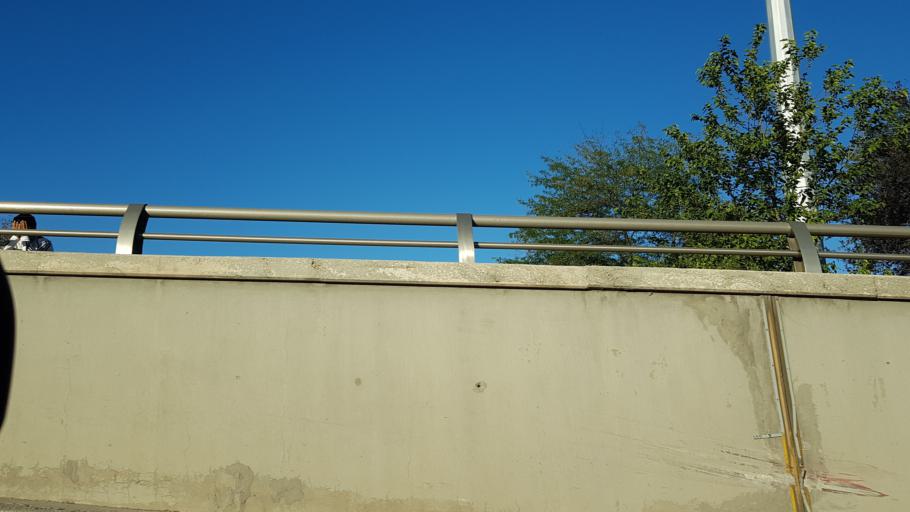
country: TR
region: Ankara
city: Ankara
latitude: 39.9523
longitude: 32.8339
